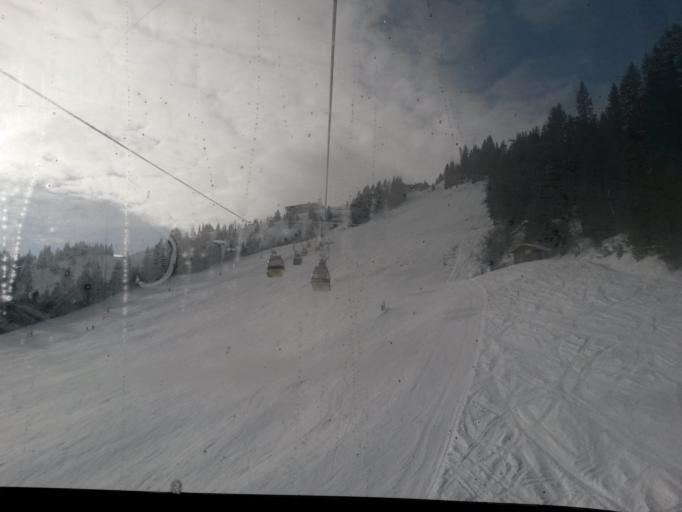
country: AT
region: Salzburg
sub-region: Politischer Bezirk Sankt Johann im Pongau
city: Dorfgastein
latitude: 47.2350
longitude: 13.1766
